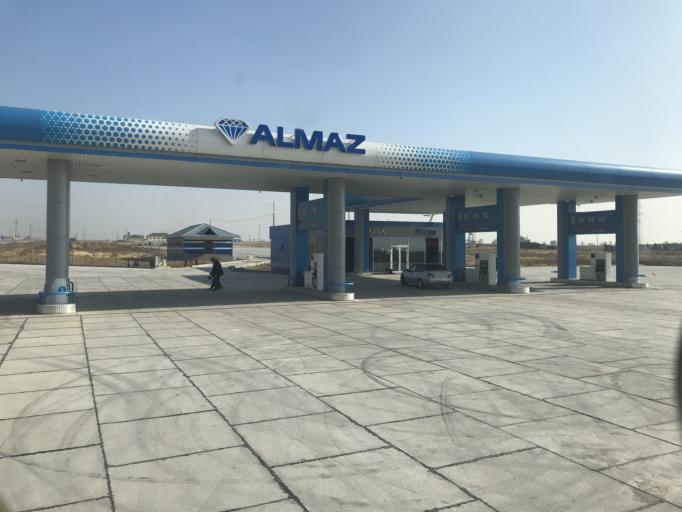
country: KZ
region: Ongtustik Qazaqstan
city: Shymkent
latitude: 42.4553
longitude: 69.6084
